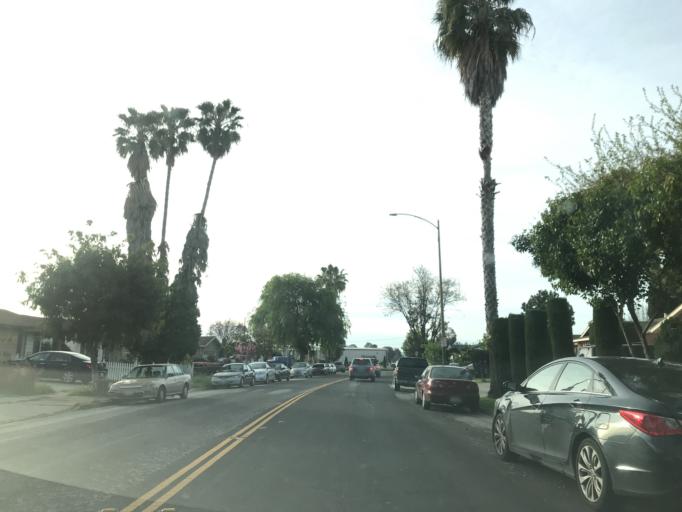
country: US
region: California
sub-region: Santa Clara County
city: Alum Rock
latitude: 37.3410
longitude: -121.8224
